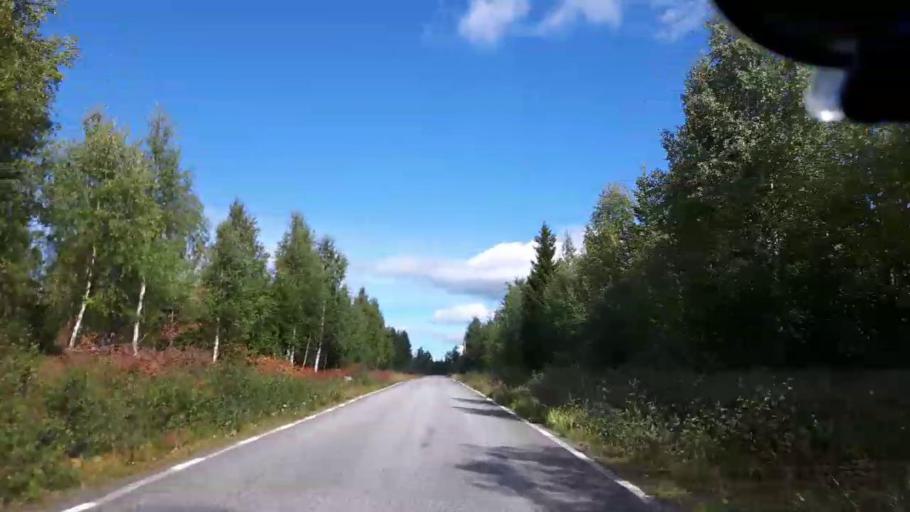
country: SE
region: Jaemtland
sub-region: OEstersunds Kommun
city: Brunflo
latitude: 63.1948
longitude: 15.2205
